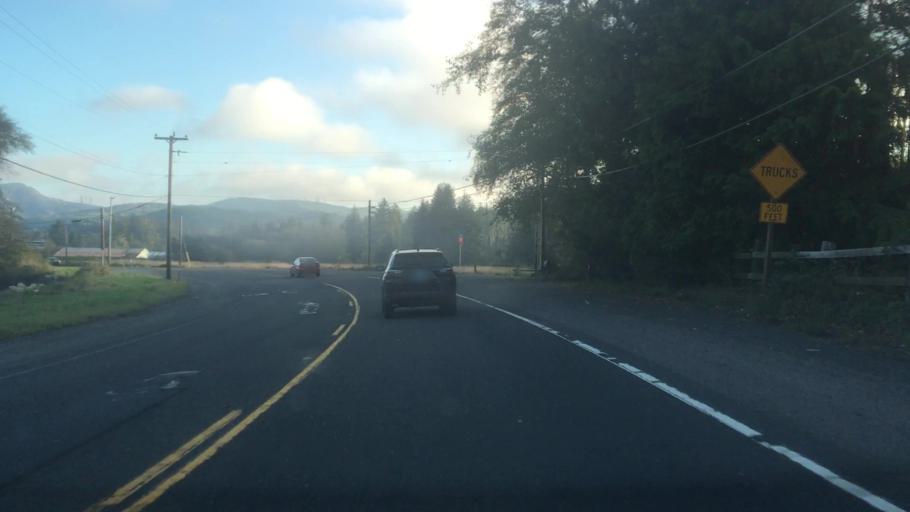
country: US
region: Oregon
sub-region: Clatsop County
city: Seaside
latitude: 45.9510
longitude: -123.9268
